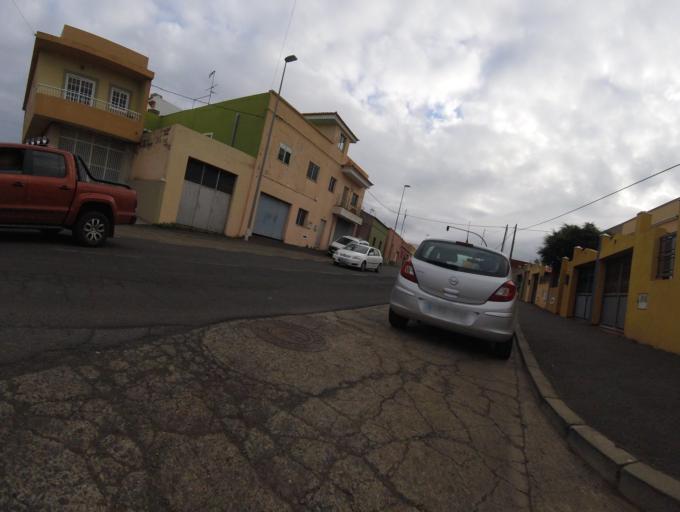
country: ES
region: Canary Islands
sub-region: Provincia de Santa Cruz de Tenerife
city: La Laguna
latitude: 28.4468
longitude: -16.3313
